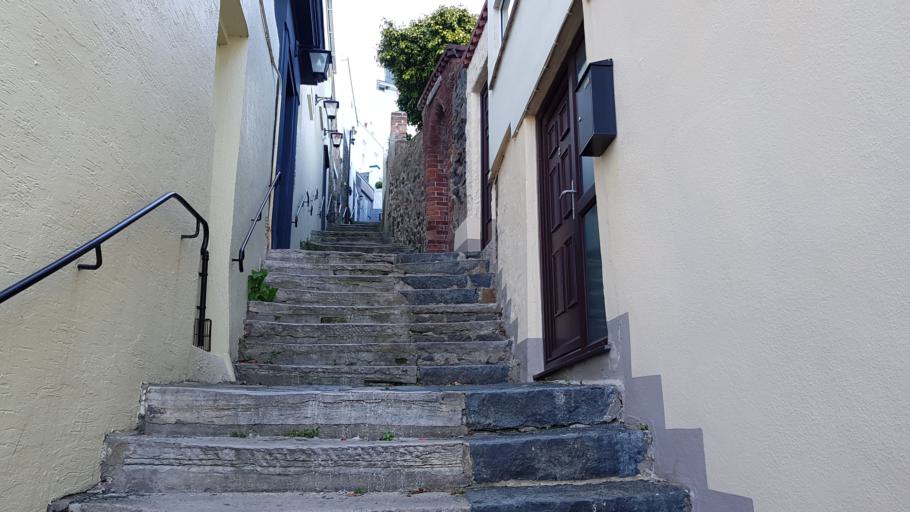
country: GG
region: St Peter Port
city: Saint Peter Port
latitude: 49.4541
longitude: -2.5384
